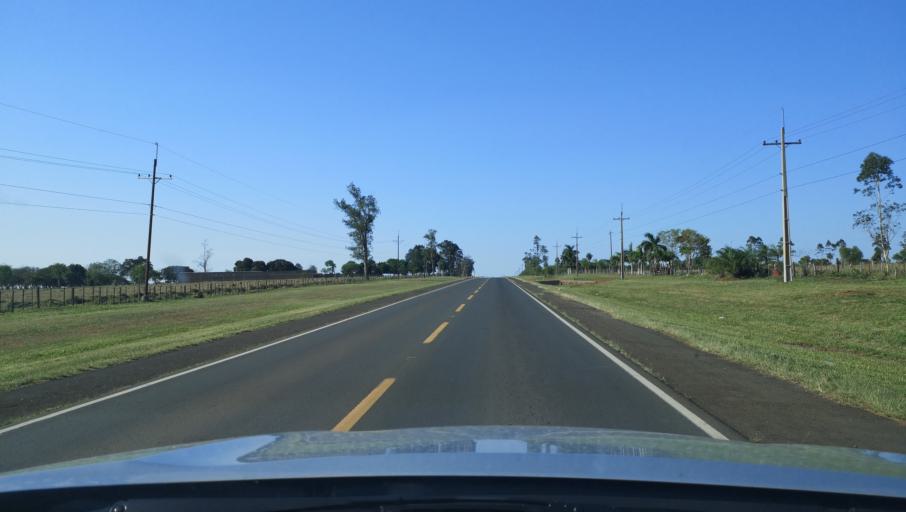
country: PY
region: Misiones
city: Santa Maria
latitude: -26.8266
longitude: -57.0293
